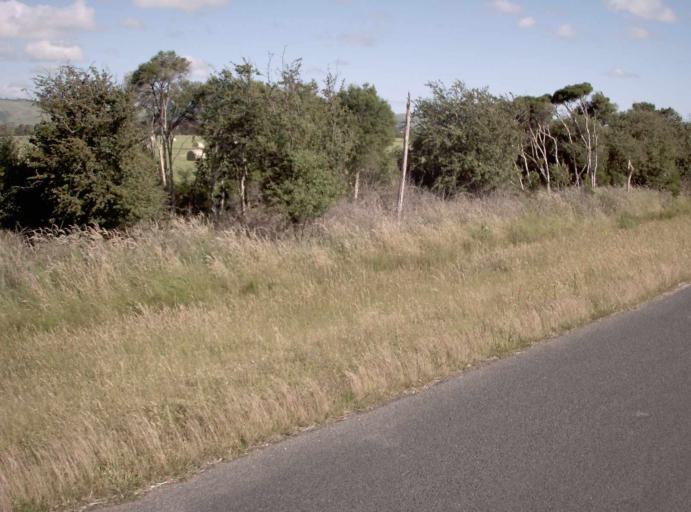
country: AU
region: Victoria
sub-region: Bass Coast
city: North Wonthaggi
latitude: -38.4463
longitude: 145.4826
